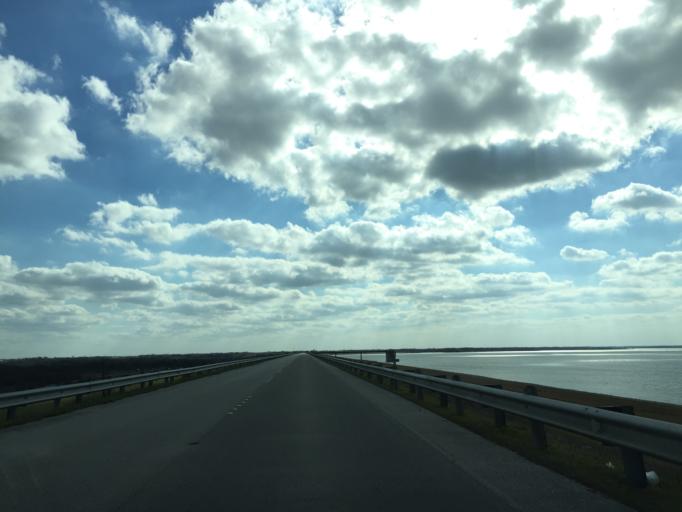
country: US
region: Texas
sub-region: Williamson County
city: Granger
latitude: 30.7087
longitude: -97.3264
